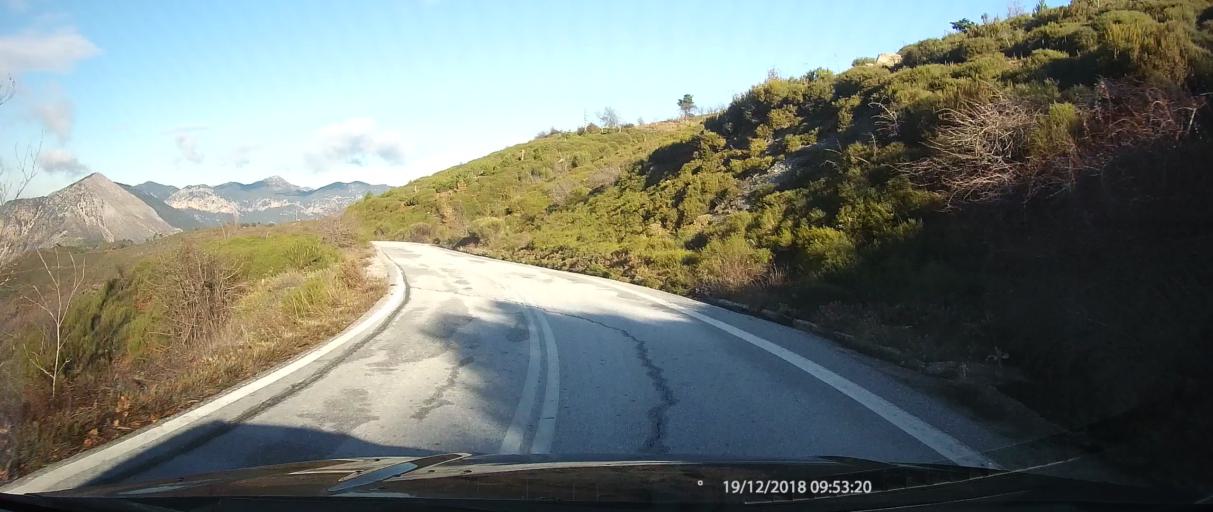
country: GR
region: Peloponnese
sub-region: Nomos Messinias
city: Paralia Vergas
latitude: 37.0715
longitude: 22.2540
